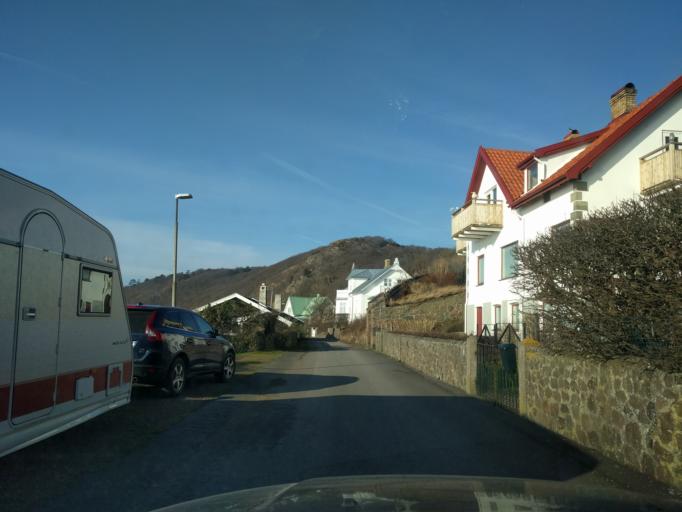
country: SE
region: Skane
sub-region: Hoganas Kommun
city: Hoganas
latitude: 56.2865
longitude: 12.4911
